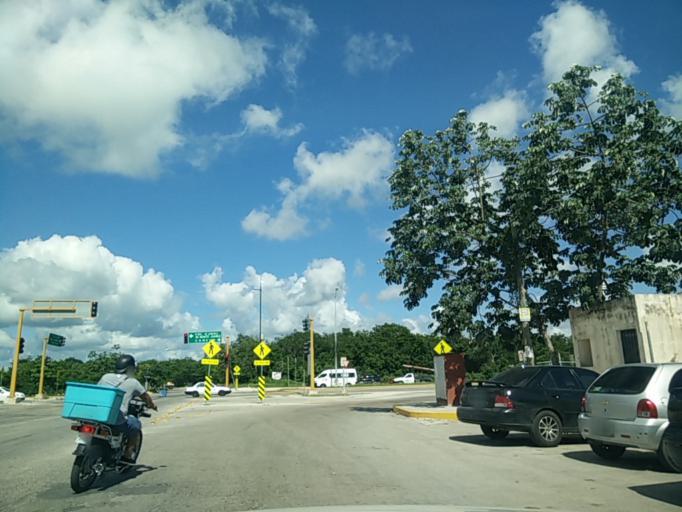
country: MX
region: Quintana Roo
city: Playa del Carmen
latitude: 20.6672
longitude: -87.0663
